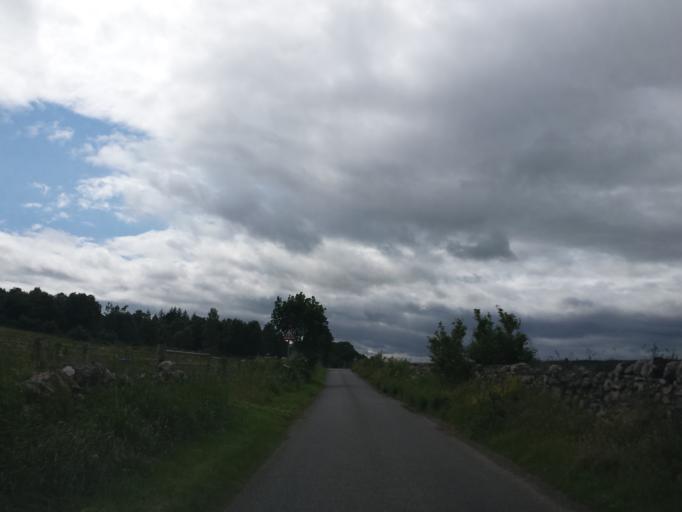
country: GB
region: Scotland
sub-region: Highland
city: Nairn
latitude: 57.5054
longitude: -3.9914
